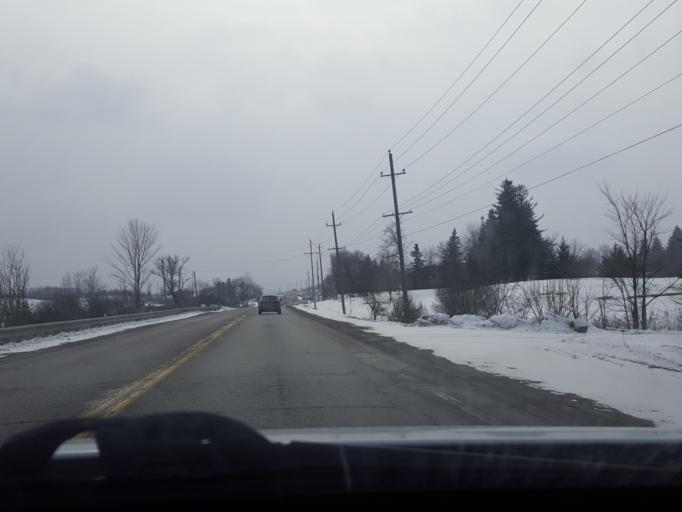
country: CA
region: Ontario
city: Uxbridge
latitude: 44.0283
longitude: -79.2122
